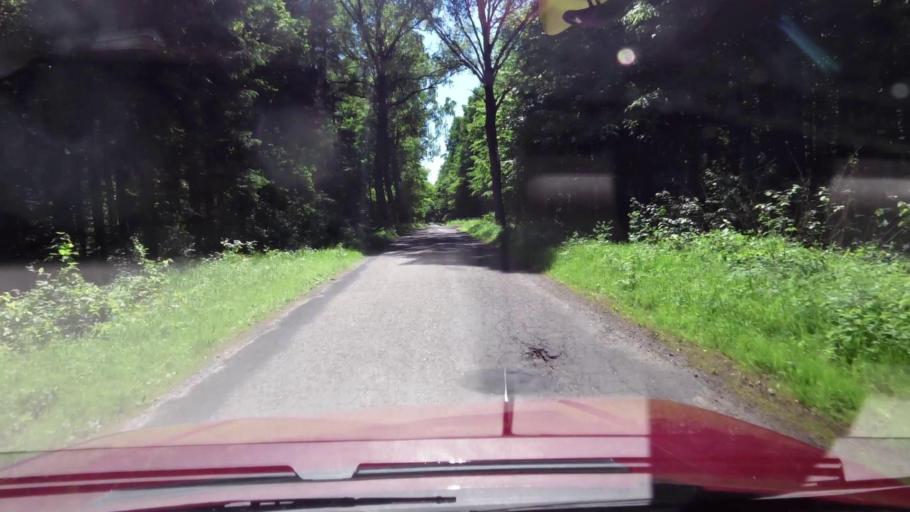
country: PL
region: West Pomeranian Voivodeship
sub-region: Powiat koszalinski
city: Bobolice
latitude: 54.0268
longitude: 16.6402
